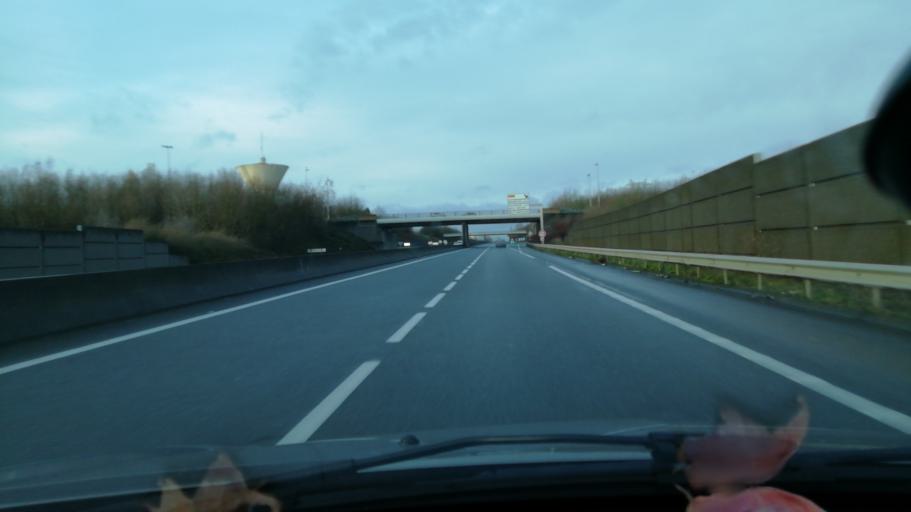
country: FR
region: Nord-Pas-de-Calais
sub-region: Departement du Nord
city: Hautmont
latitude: 50.2652
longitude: 3.9249
